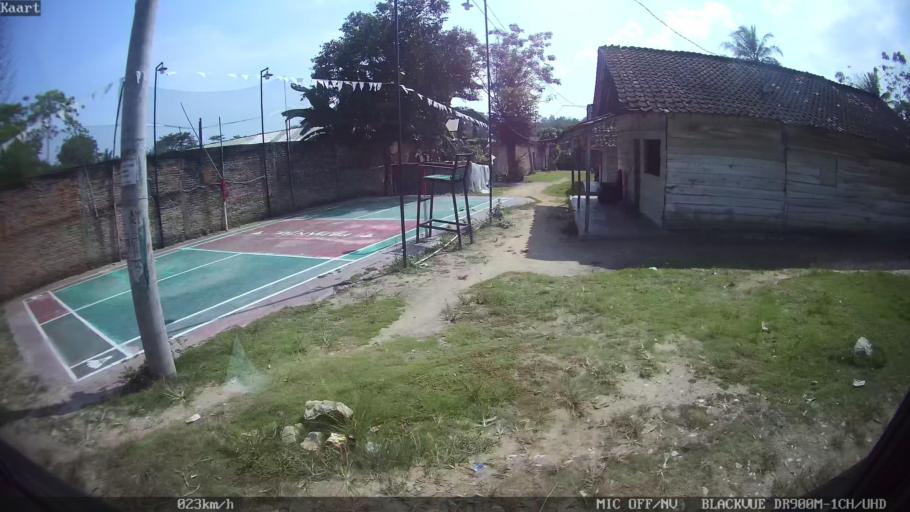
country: ID
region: Lampung
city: Natar
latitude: -5.2557
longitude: 105.1960
